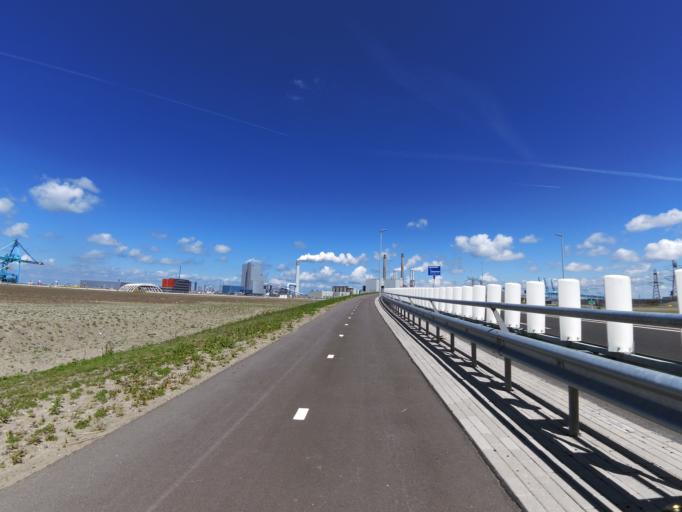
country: NL
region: South Holland
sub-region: Gemeente Rotterdam
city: Hoek van Holland
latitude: 51.9507
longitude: 4.0146
